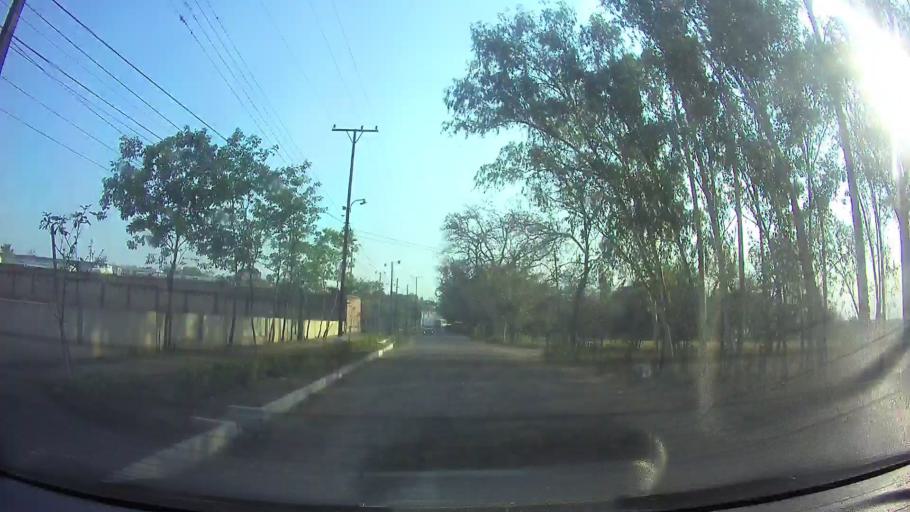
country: PY
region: Central
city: Limpio
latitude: -25.2243
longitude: -57.5070
